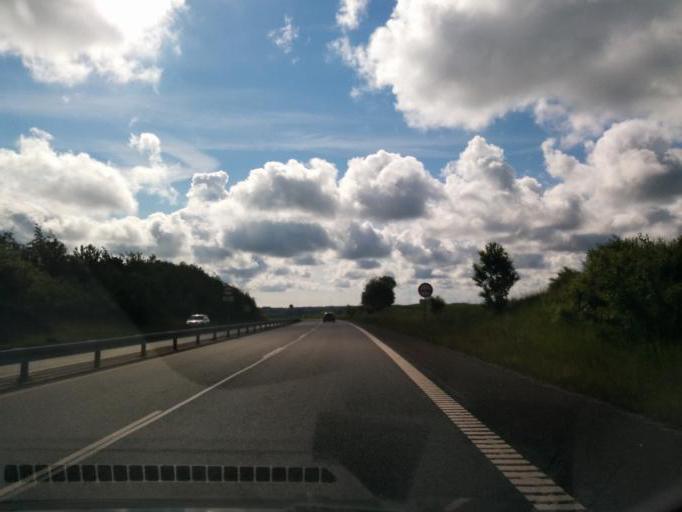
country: DK
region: Central Jutland
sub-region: Syddjurs Kommune
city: Ronde
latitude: 56.2977
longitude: 10.5164
